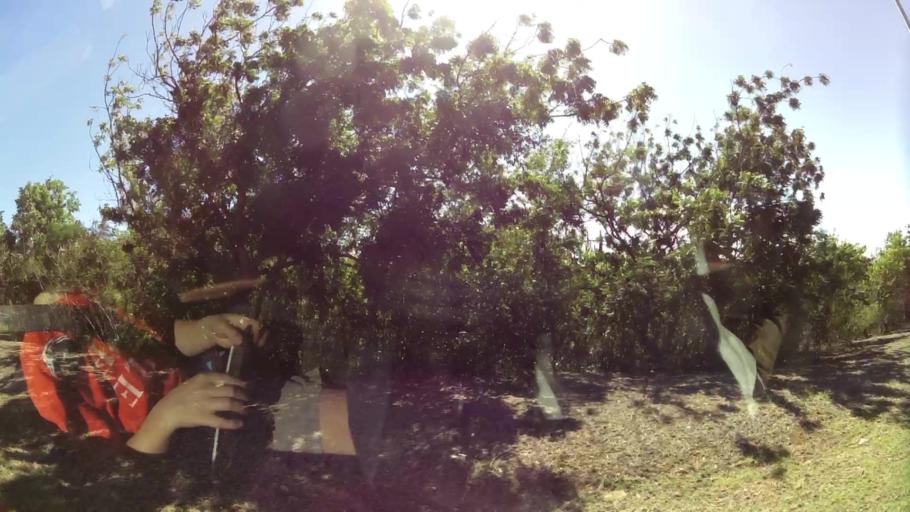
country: AG
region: Saint Paul
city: Falmouth
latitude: 17.0091
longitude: -61.7566
